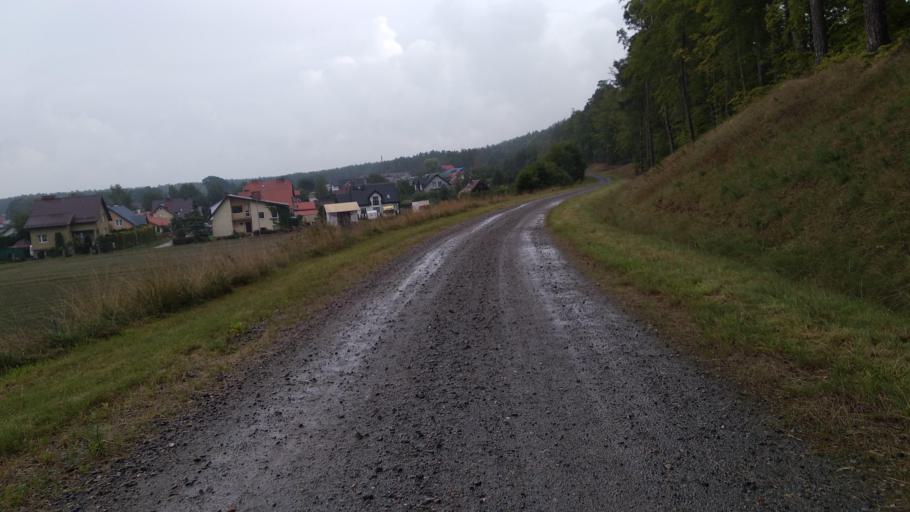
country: PL
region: Pomeranian Voivodeship
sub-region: Powiat wejherowski
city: Goscicino
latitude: 54.6325
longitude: 18.1363
